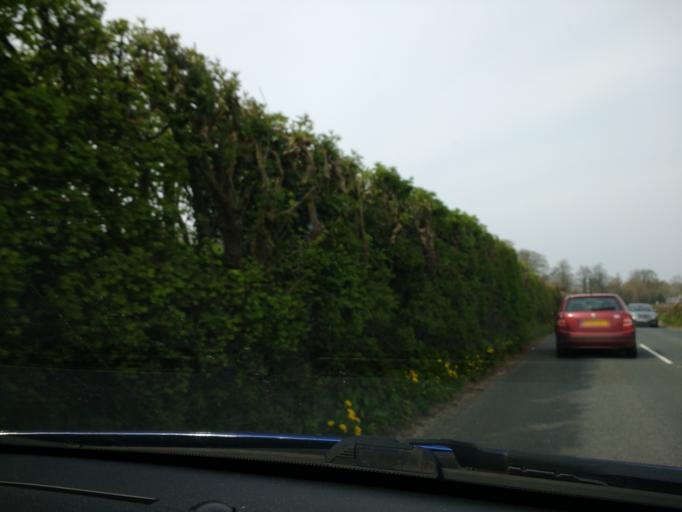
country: GB
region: England
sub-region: Lancashire
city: Lancaster
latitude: 54.0212
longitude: -2.8098
